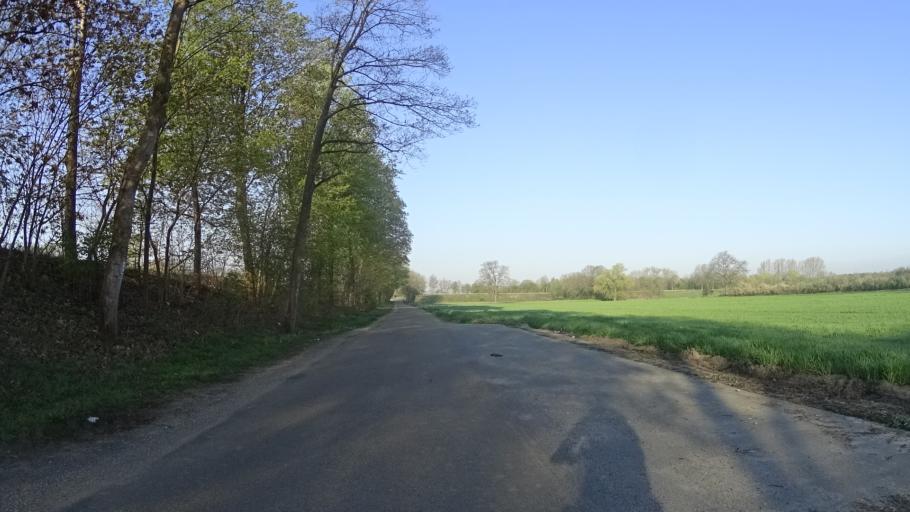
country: DE
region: North Rhine-Westphalia
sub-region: Regierungsbezirk Dusseldorf
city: Hunxe
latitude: 51.6486
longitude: 6.7654
